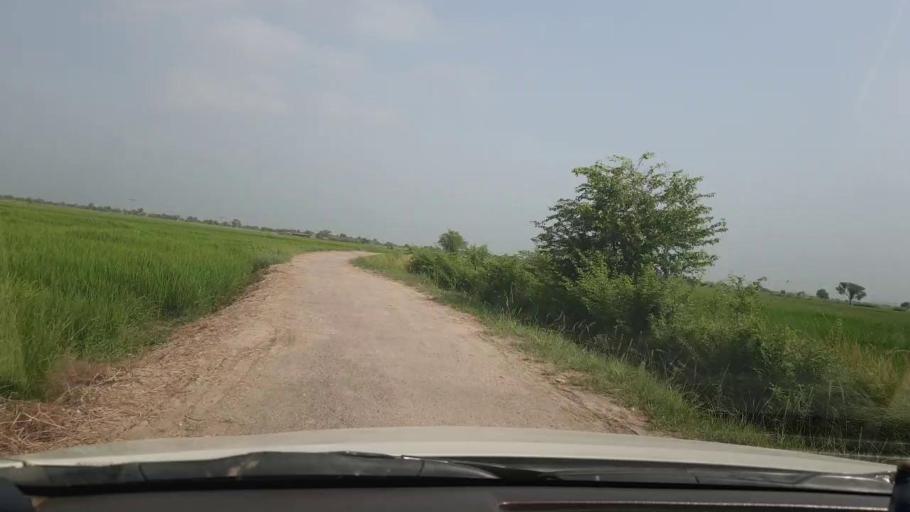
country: PK
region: Sindh
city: Shikarpur
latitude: 27.9855
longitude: 68.6092
